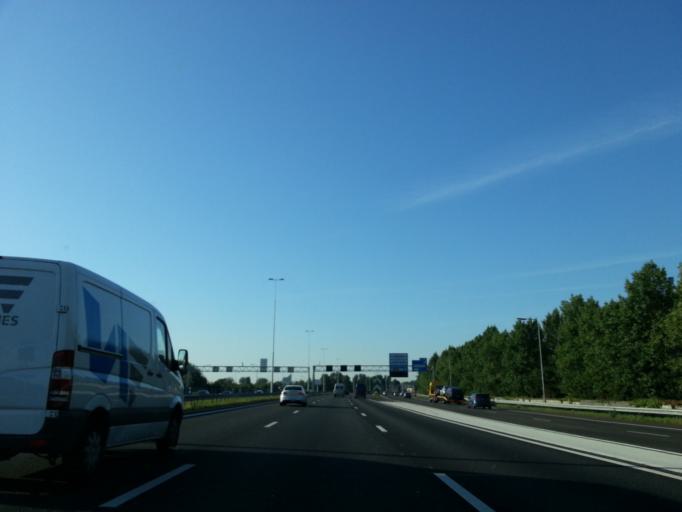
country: NL
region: South Holland
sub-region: Gemeente Rotterdam
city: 's-Gravenland
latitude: 51.9319
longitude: 4.5375
